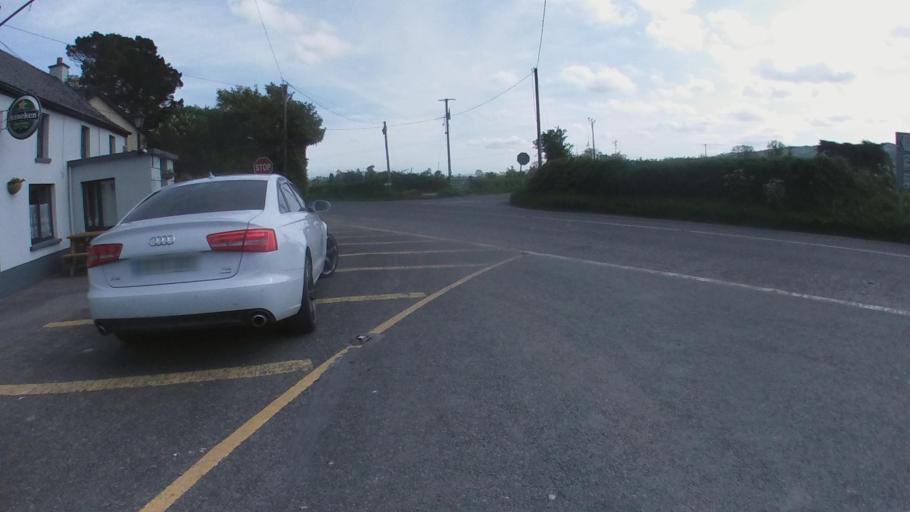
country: IE
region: Leinster
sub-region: County Carlow
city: Carlow
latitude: 52.8427
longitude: -6.9775
